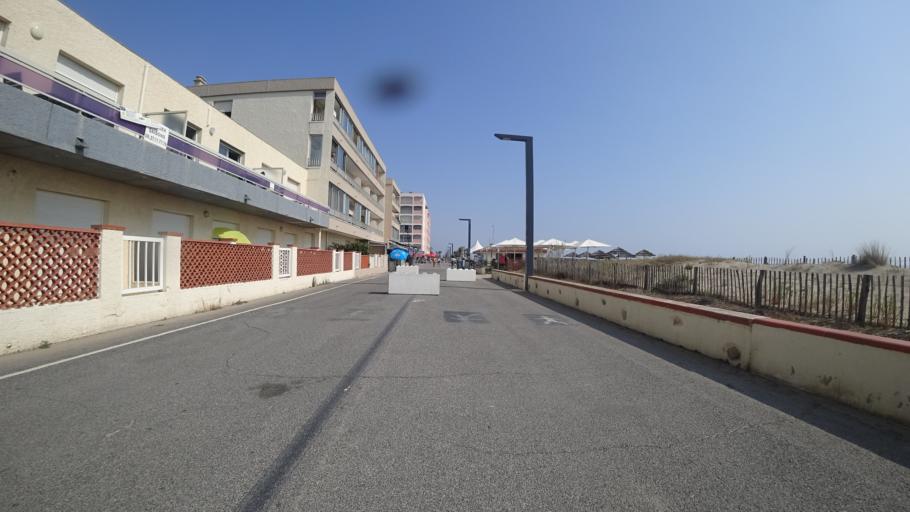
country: FR
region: Languedoc-Roussillon
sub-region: Departement des Pyrenees-Orientales
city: Saint-Cyprien-Plage
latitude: 42.6285
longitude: 3.0358
